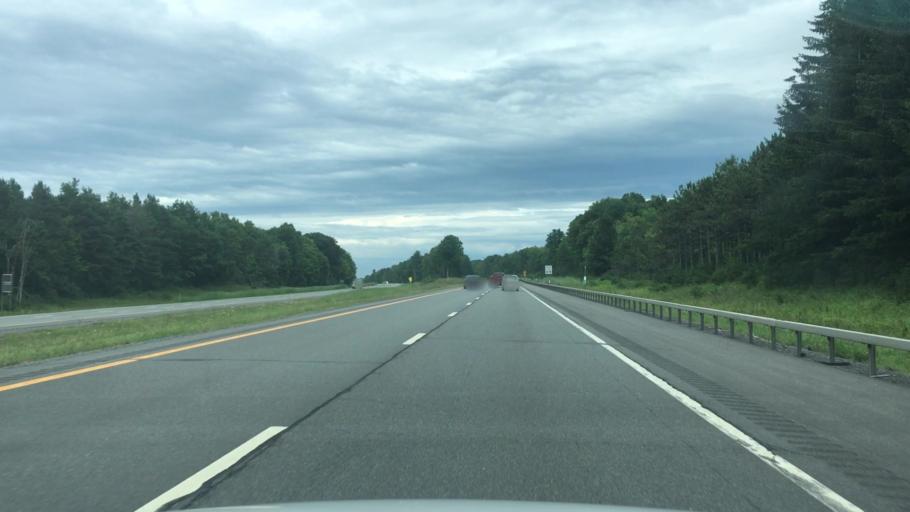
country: US
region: New York
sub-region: Schoharie County
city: Schoharie
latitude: 42.7237
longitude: -74.2320
